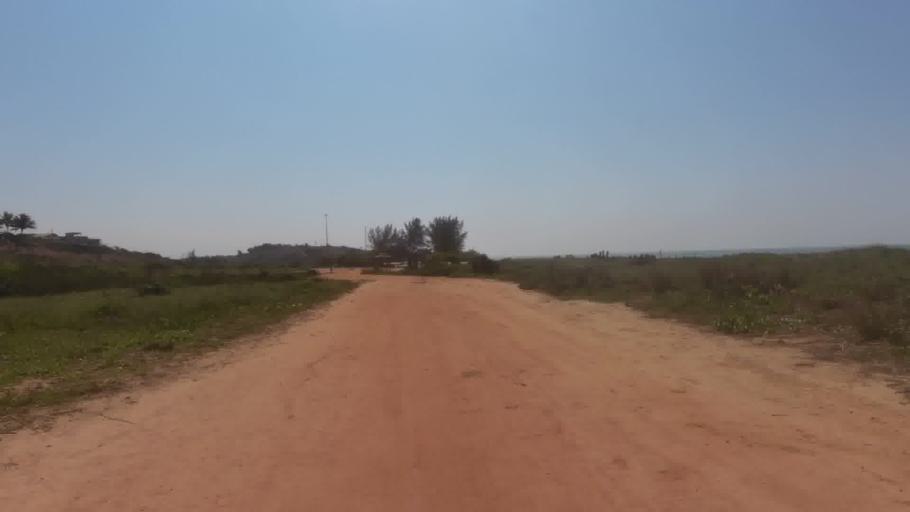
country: BR
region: Espirito Santo
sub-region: Marataizes
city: Marataizes
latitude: -21.1119
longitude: -40.8540
